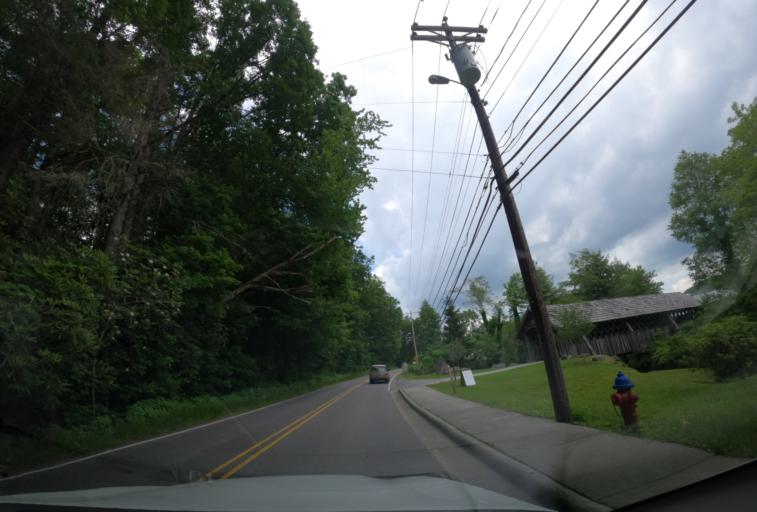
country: US
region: North Carolina
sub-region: Macon County
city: Franklin
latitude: 35.0564
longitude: -83.2053
